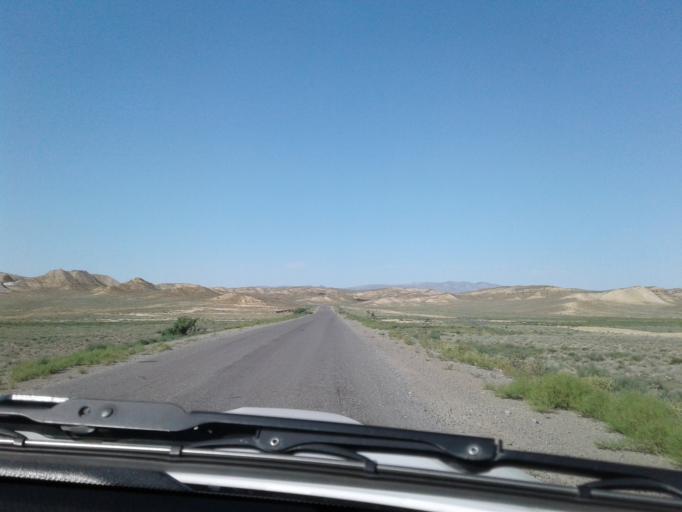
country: TM
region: Balkan
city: Magtymguly
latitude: 38.6696
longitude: 56.2901
